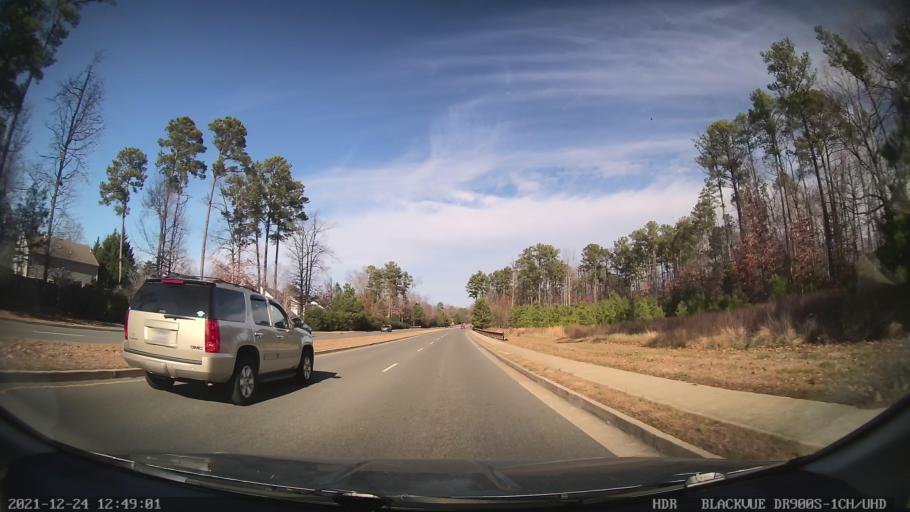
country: US
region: Virginia
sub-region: Henrico County
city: Short Pump
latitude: 37.6372
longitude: -77.6127
